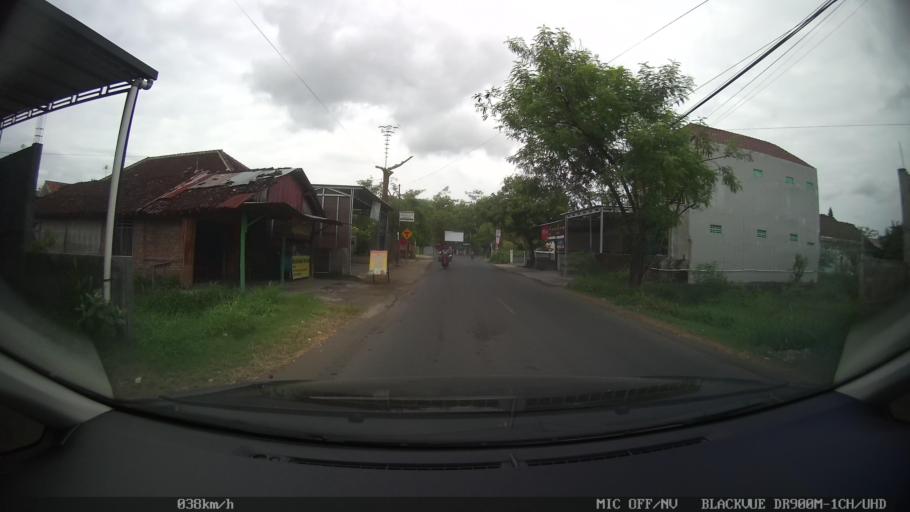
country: ID
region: Daerah Istimewa Yogyakarta
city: Sewon
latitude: -7.8750
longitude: 110.4071
